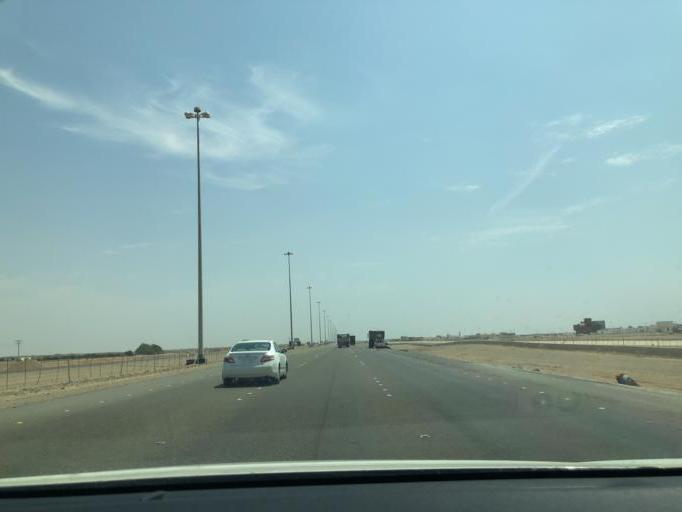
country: SA
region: Makkah
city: Rabigh
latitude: 22.2662
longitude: 39.1220
